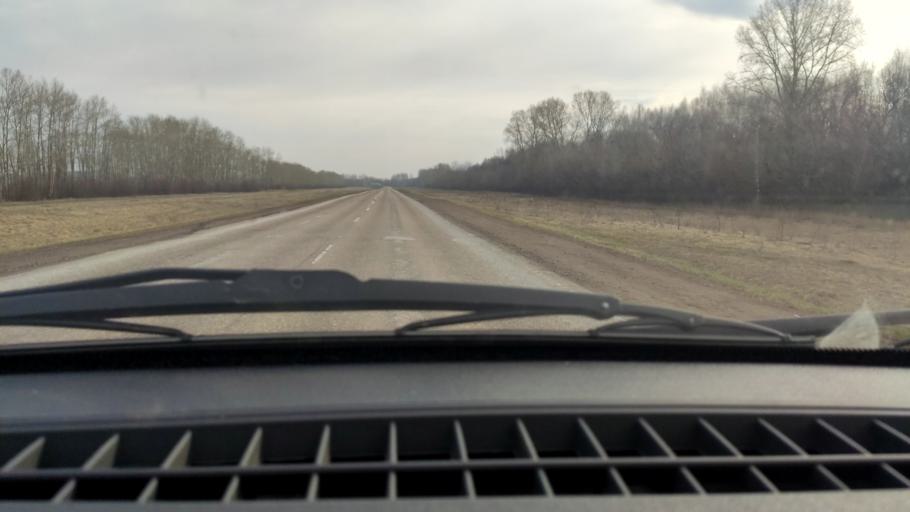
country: RU
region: Bashkortostan
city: Davlekanovo
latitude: 54.3545
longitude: 55.1848
